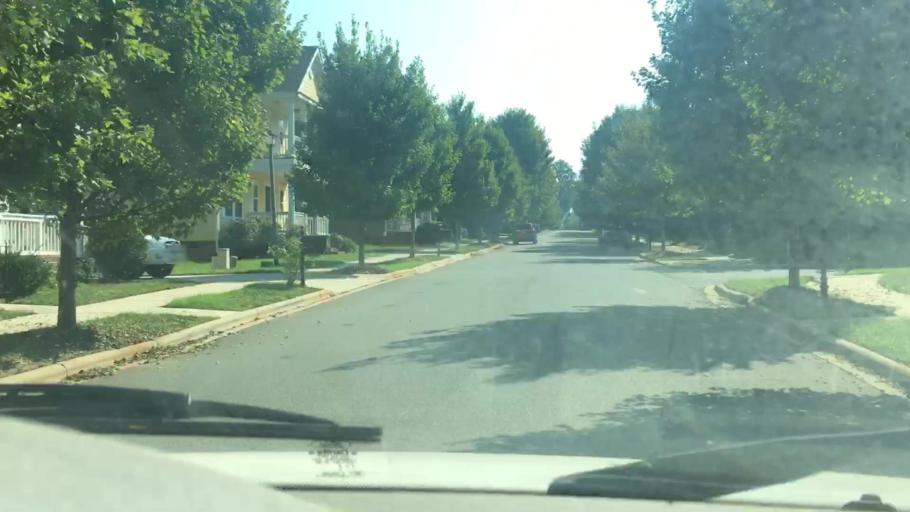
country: US
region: North Carolina
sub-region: Mecklenburg County
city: Huntersville
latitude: 35.4308
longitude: -80.8540
